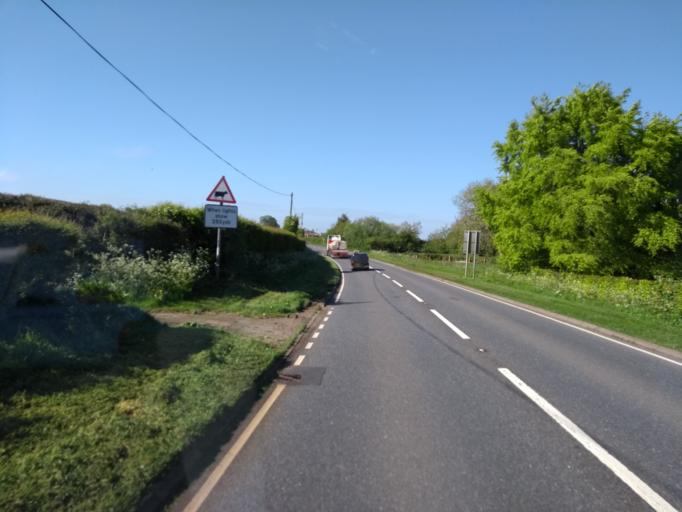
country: GB
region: England
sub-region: Devon
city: Honiton
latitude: 50.8707
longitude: -3.1011
